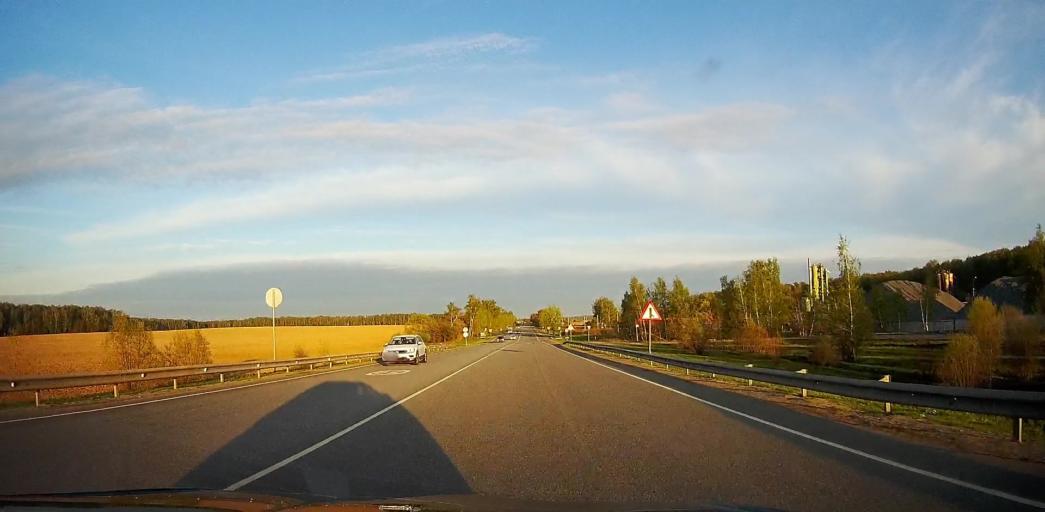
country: RU
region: Moskovskaya
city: Troitskoye
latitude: 55.2167
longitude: 38.5898
